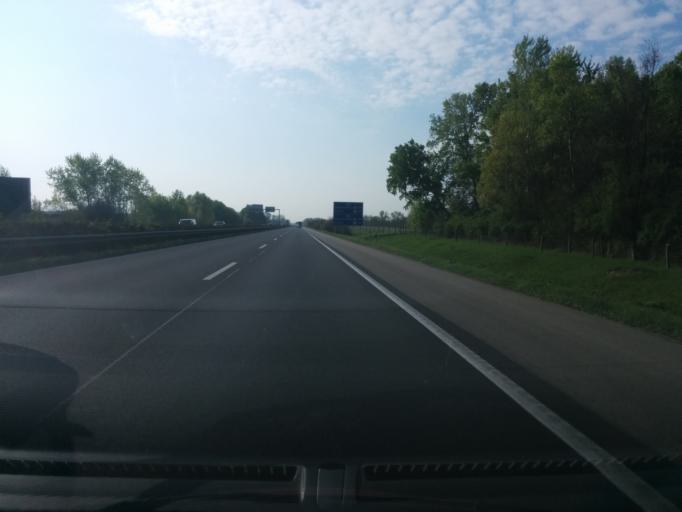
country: HU
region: Pest
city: Gyal
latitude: 47.3849
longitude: 19.1764
